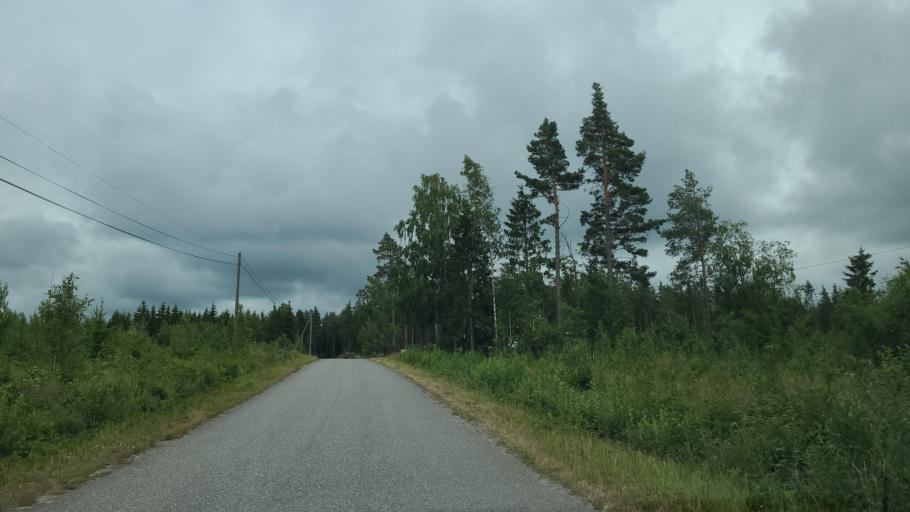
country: FI
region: Varsinais-Suomi
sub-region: Aboland-Turunmaa
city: Dragsfjaerd
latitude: 60.0810
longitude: 22.4166
